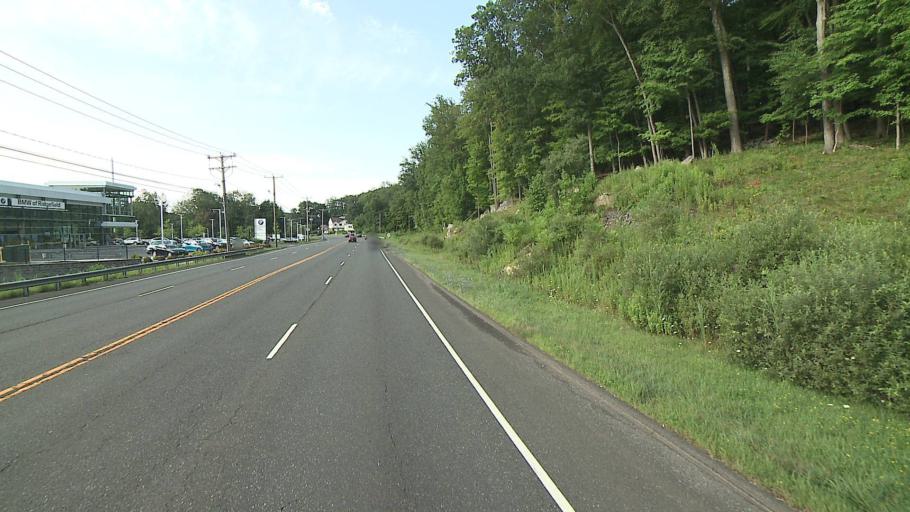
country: US
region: Connecticut
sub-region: Fairfield County
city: Ridgefield
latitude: 41.3316
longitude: -73.4729
